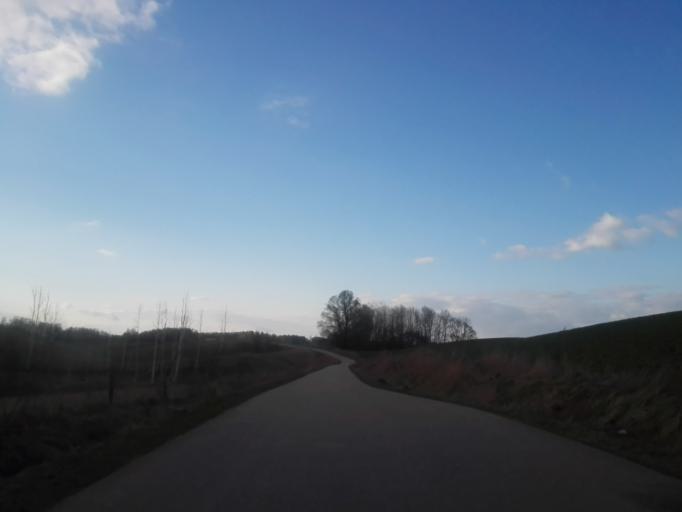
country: PL
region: Podlasie
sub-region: Suwalki
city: Suwalki
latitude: 54.2091
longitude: 23.0088
